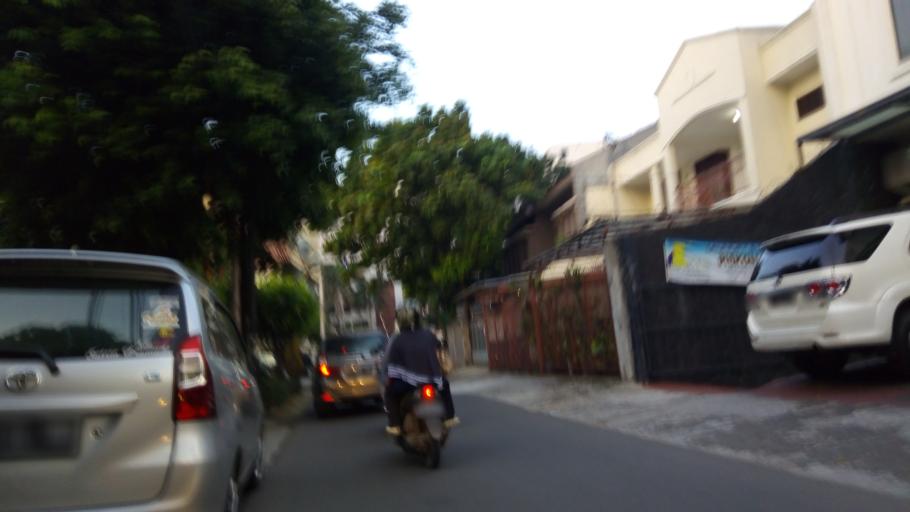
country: ID
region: Jakarta Raya
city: Jakarta
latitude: -6.2448
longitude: 106.7962
